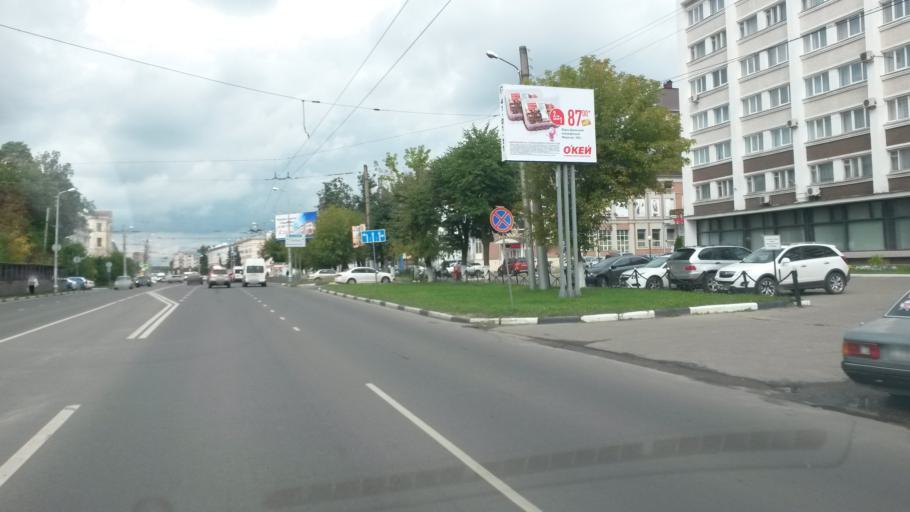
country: RU
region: Ivanovo
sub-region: Gorod Ivanovo
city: Ivanovo
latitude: 57.0088
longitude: 40.9725
